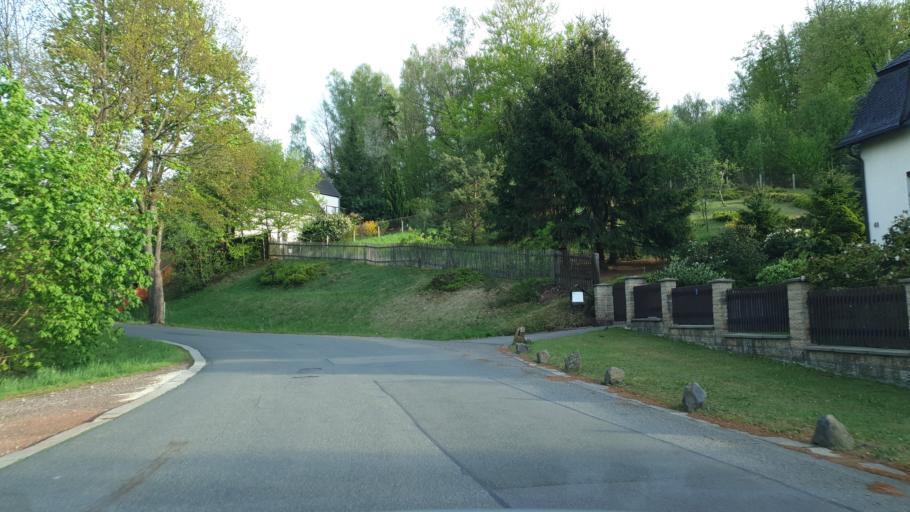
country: DE
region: Saxony
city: Oelsnitz
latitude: 50.7324
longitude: 12.6881
